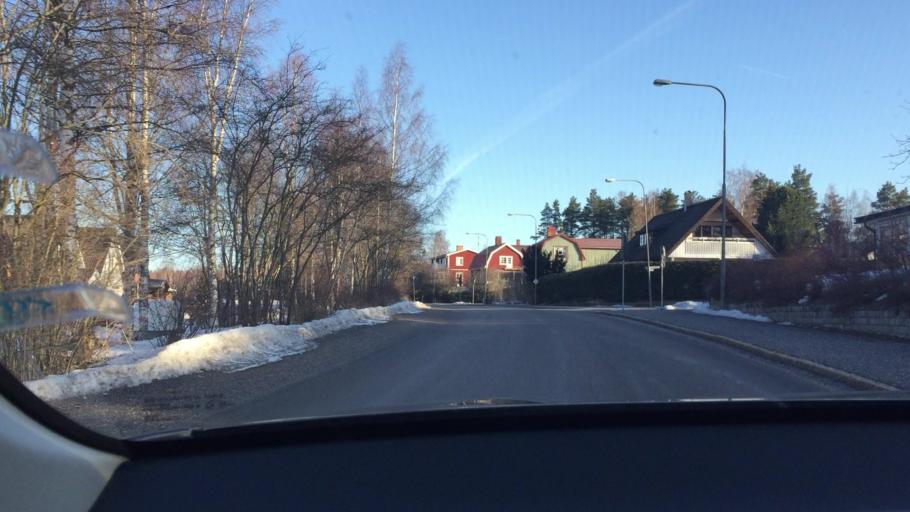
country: SE
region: Dalarna
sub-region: Faluns Kommun
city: Falun
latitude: 60.5726
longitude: 15.6508
